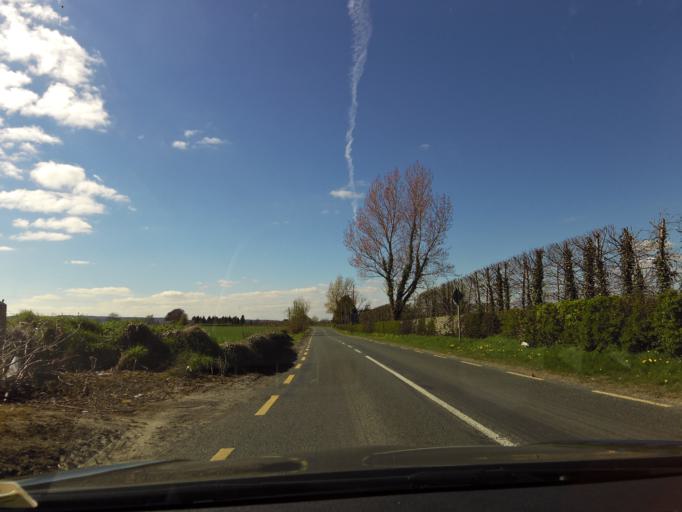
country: IE
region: Leinster
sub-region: Kildare
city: Athy
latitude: 52.9988
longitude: -7.0001
